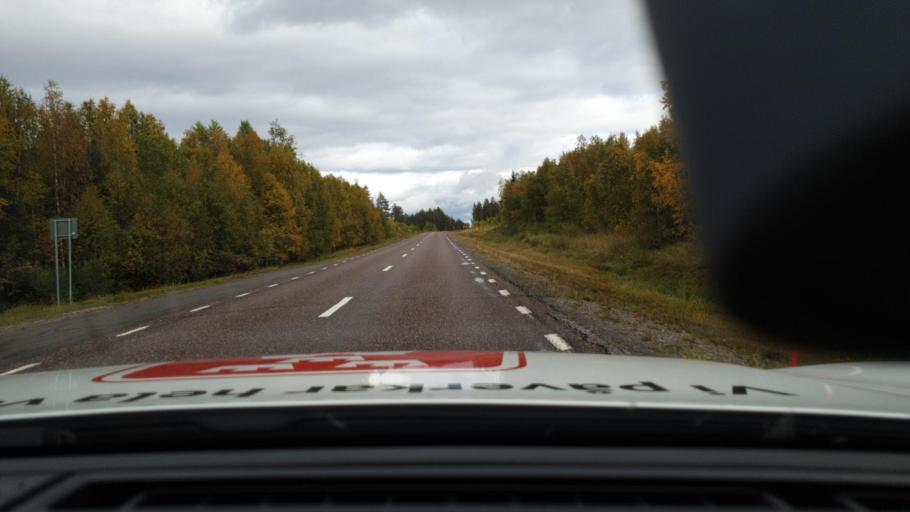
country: SE
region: Norrbotten
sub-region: Gallivare Kommun
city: Gaellivare
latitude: 67.0302
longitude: 21.7387
